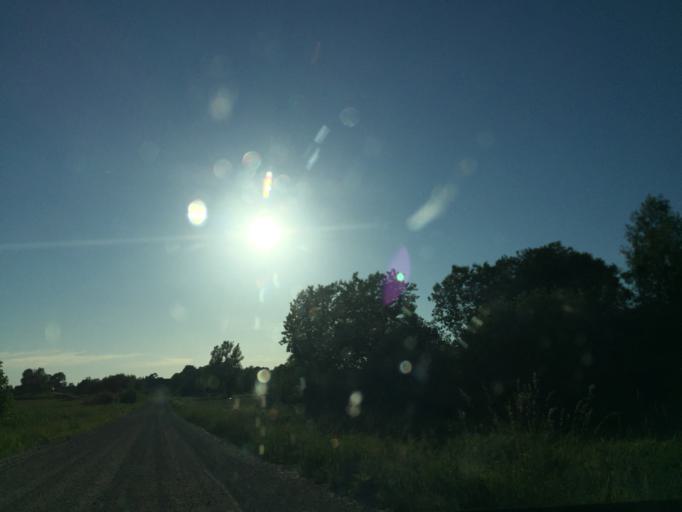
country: LV
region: Broceni
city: Broceni
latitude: 56.8644
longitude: 22.5928
